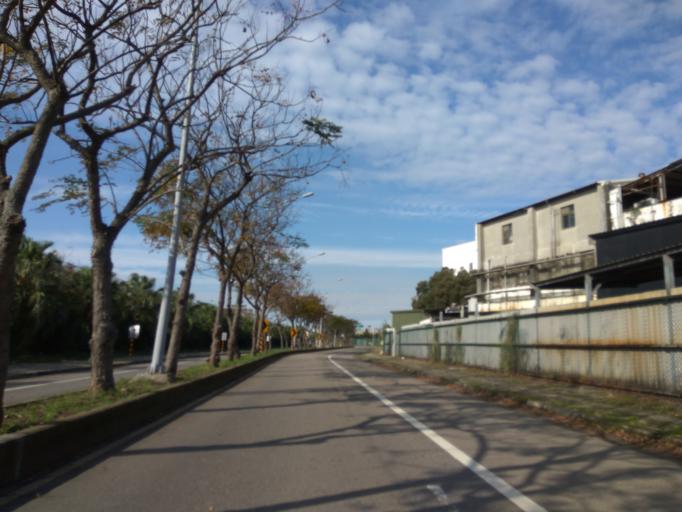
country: TW
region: Taiwan
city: Taoyuan City
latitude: 25.0570
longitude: 121.1802
